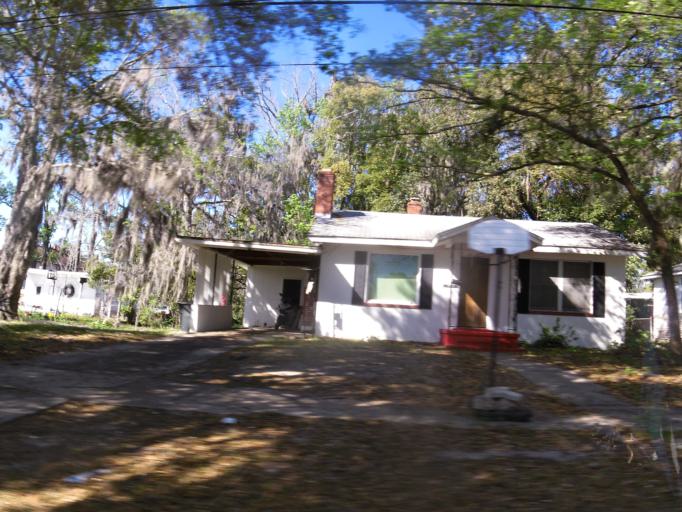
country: US
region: Florida
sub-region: Duval County
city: Jacksonville
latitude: 30.3598
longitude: -81.6517
